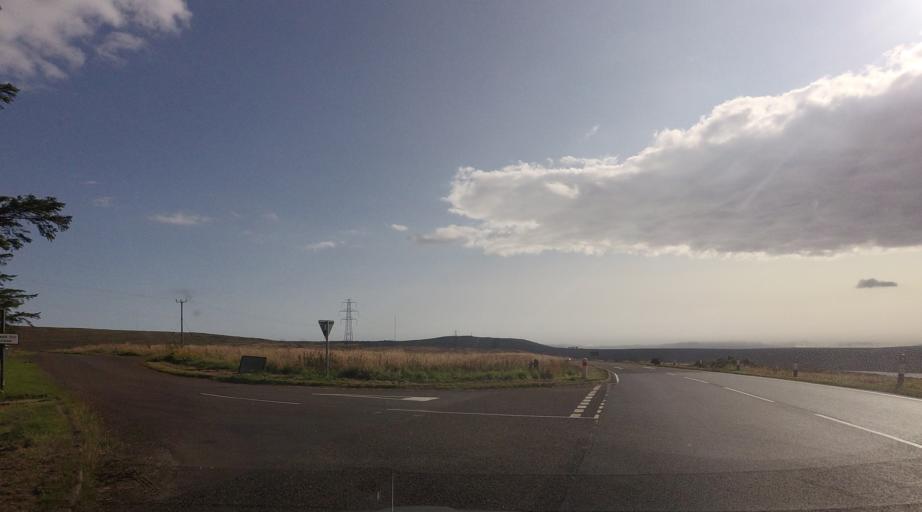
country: GB
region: Scotland
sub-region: Highland
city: Thurso
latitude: 58.3646
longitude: -3.4037
